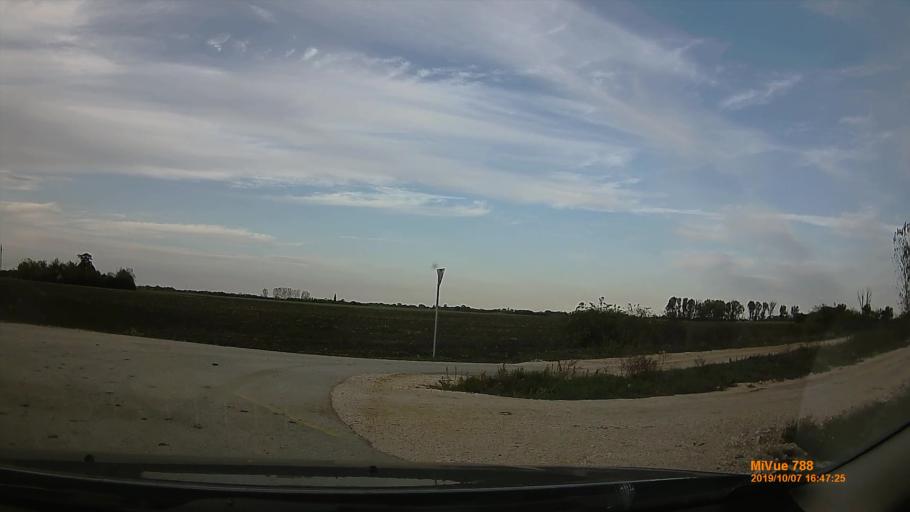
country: HU
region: Bekes
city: Szarvas
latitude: 46.8211
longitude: 20.6045
